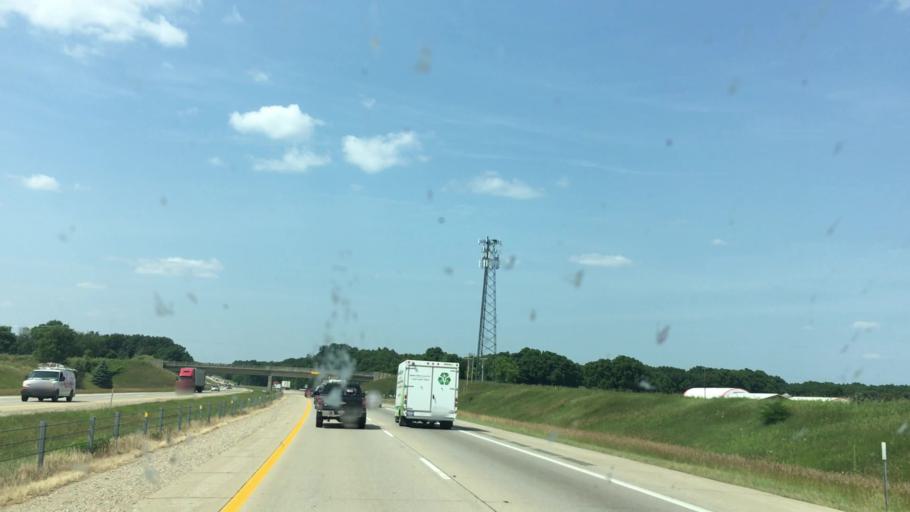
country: US
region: Michigan
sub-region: Allegan County
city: Plainwell
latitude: 42.4908
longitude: -85.6517
